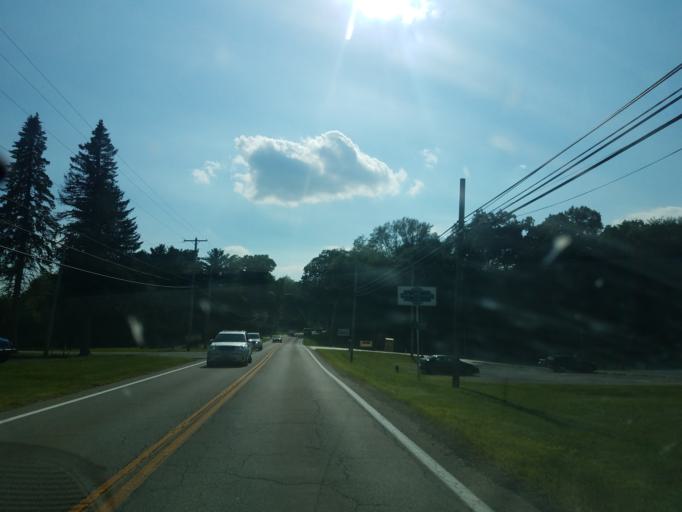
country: US
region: Ohio
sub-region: Stark County
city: Uniontown
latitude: 40.9768
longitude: -81.3954
